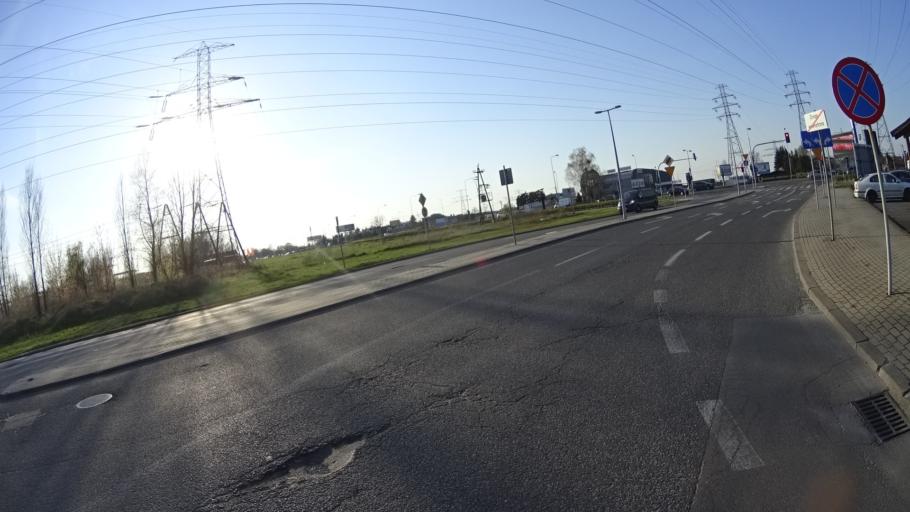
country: PL
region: Masovian Voivodeship
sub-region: Warszawa
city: Ursus
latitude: 52.2158
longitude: 20.8806
